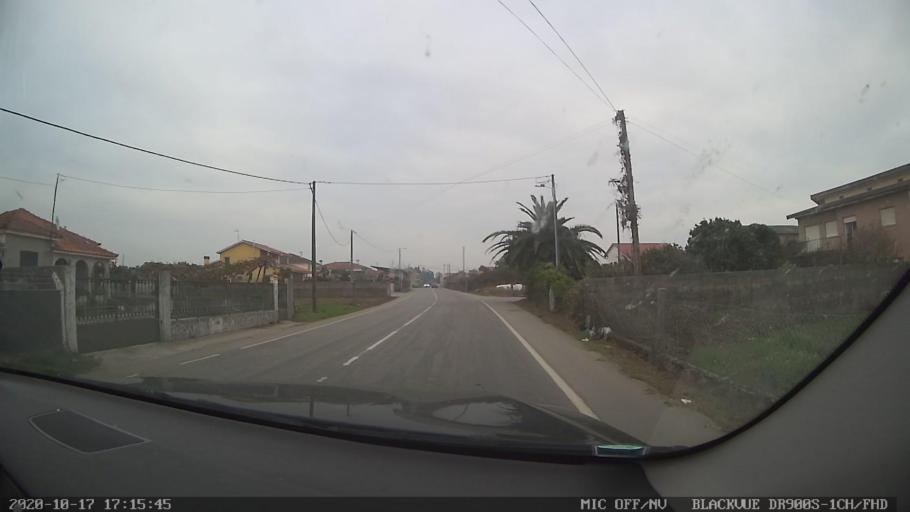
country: PT
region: Braga
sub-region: Esposende
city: Apulia
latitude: 41.4893
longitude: -8.7527
